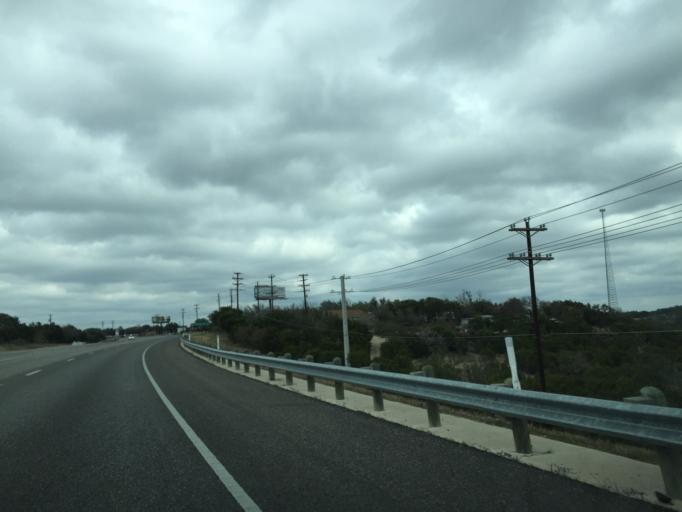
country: US
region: Texas
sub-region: Travis County
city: Briarcliff
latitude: 30.3597
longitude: -98.0690
